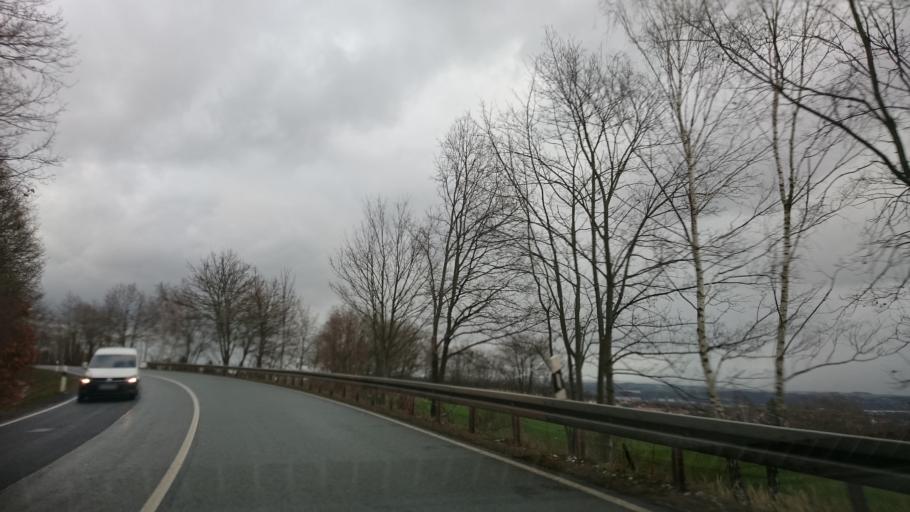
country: DE
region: Saxony
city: Hartmannsdorf
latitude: 50.7294
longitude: 12.4268
